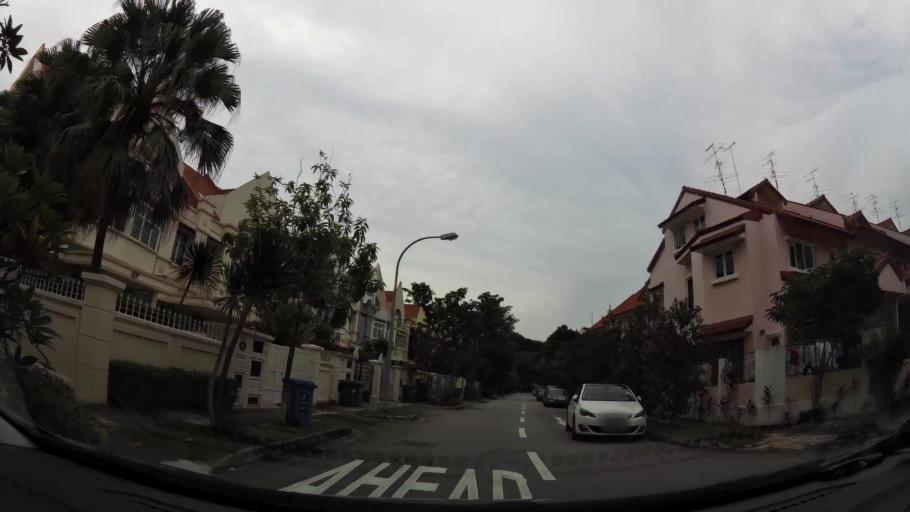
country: SG
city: Singapore
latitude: 1.3599
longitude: 103.8673
